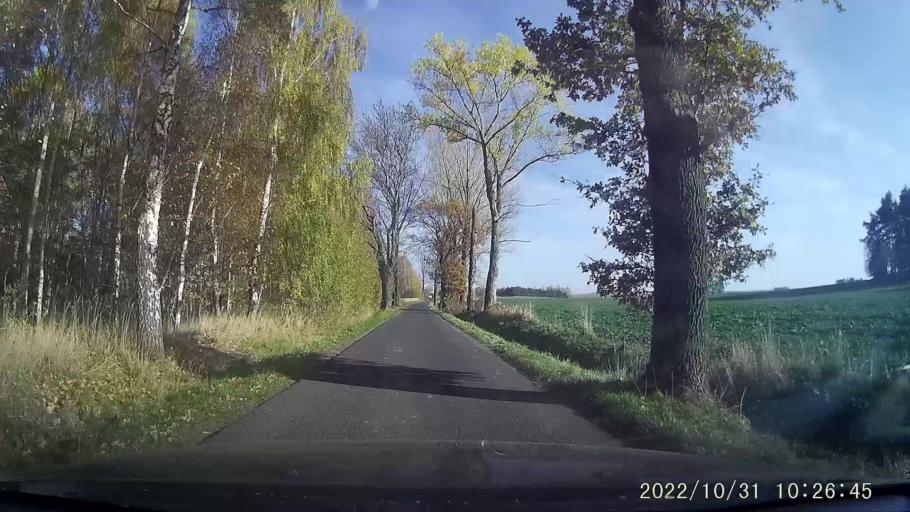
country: PL
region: Lower Silesian Voivodeship
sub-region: Powiat lubanski
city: Luban
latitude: 51.1282
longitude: 15.2873
